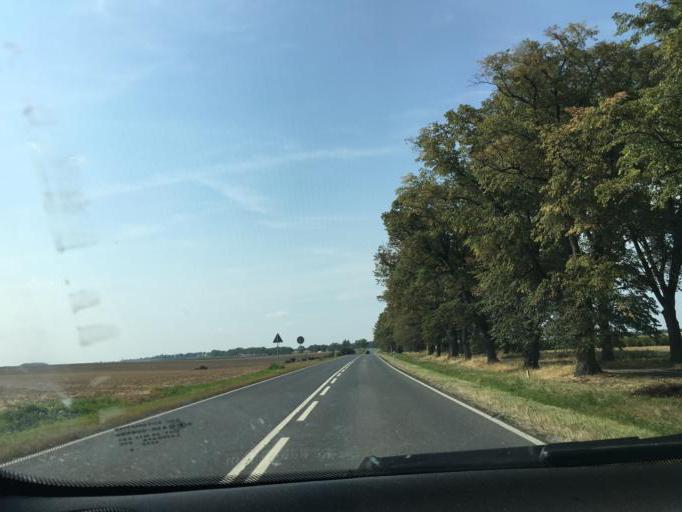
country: PL
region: Opole Voivodeship
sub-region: Powiat prudnicki
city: Laka Prudnicka
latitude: 50.4142
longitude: 17.4917
